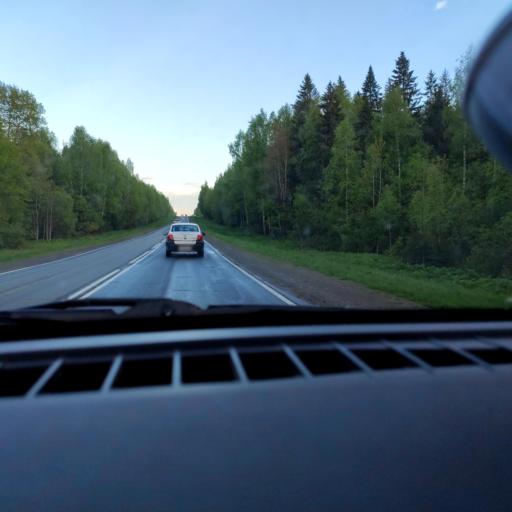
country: RU
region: Perm
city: Perm
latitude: 58.1497
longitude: 56.2580
